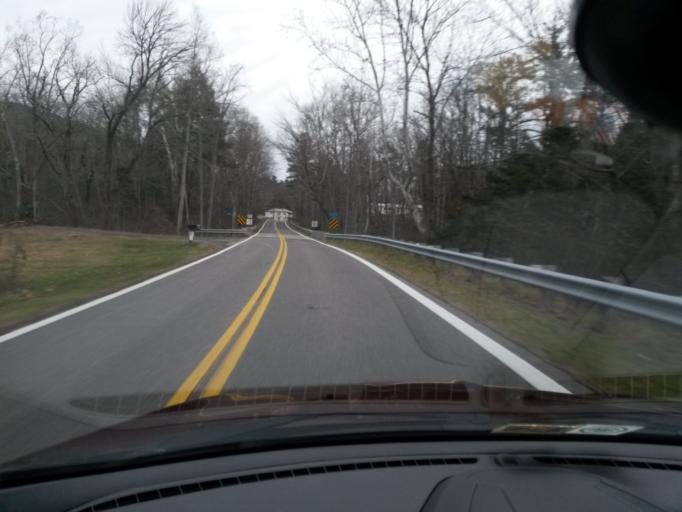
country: US
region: Virginia
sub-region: Alleghany County
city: Clifton Forge
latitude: 37.7951
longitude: -79.7097
